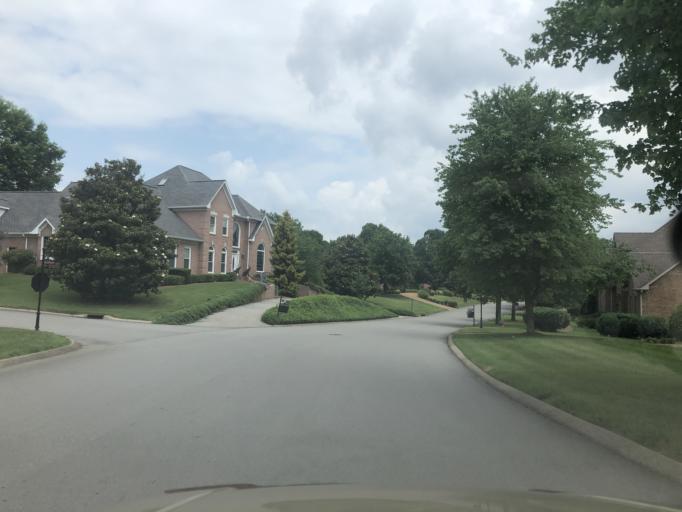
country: US
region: Tennessee
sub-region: Davidson County
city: Lakewood
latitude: 36.2387
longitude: -86.6064
